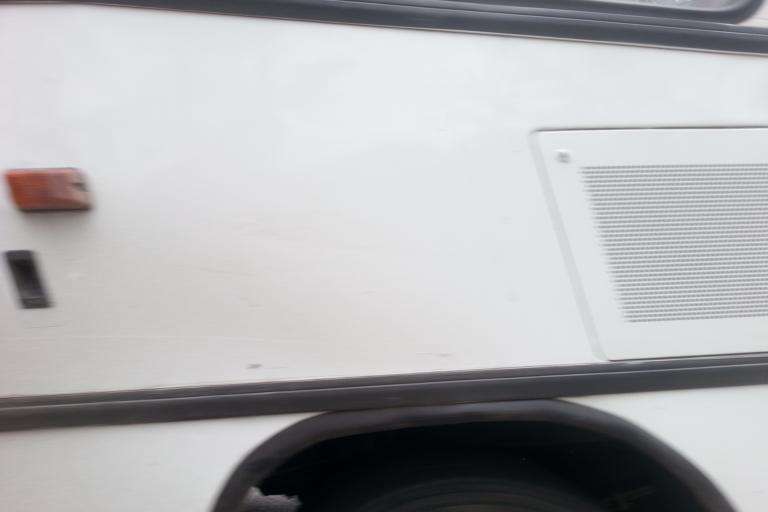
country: RU
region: Altai Krai
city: Yuzhnyy
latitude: 53.3179
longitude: 83.7062
